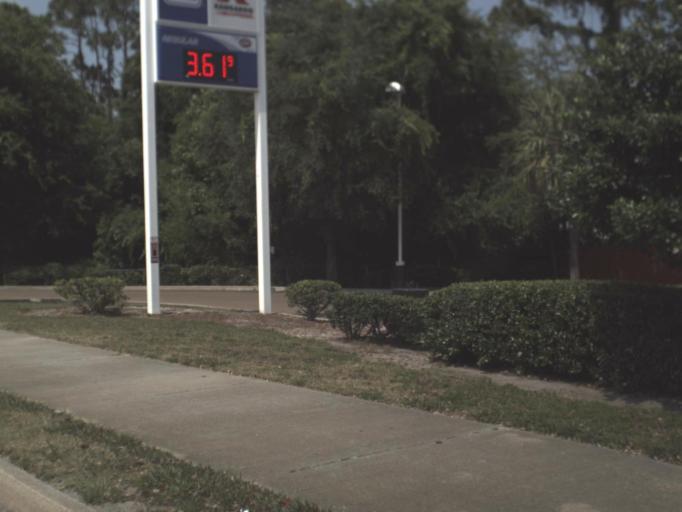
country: US
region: Florida
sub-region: Duval County
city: Atlantic Beach
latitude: 30.3545
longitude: -81.4136
